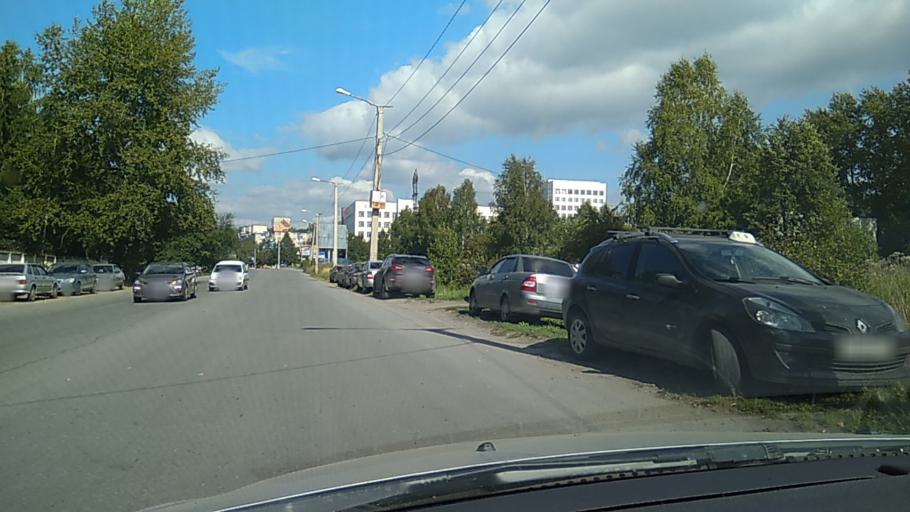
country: RU
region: Chelyabinsk
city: Zlatoust
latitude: 55.1122
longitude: 59.7046
